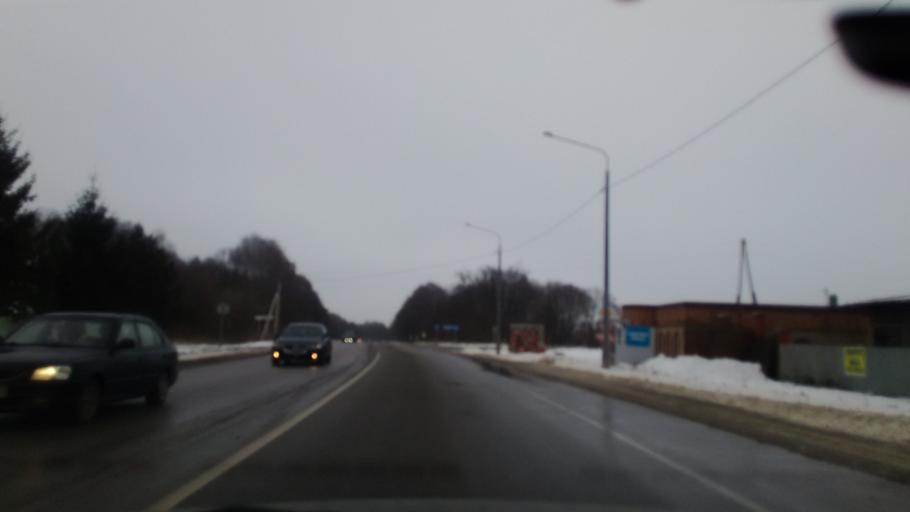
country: RU
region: Tula
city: Bolokhovo
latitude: 54.0483
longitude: 37.8301
